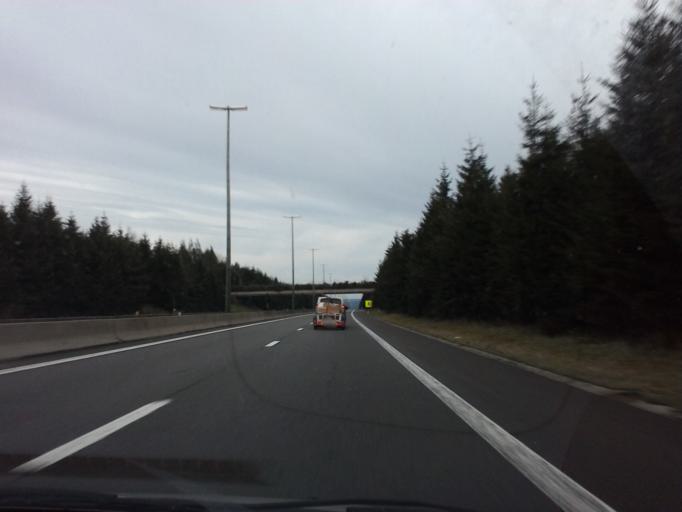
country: BE
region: Wallonia
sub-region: Province du Luxembourg
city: Manhay
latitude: 50.2599
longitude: 5.7251
